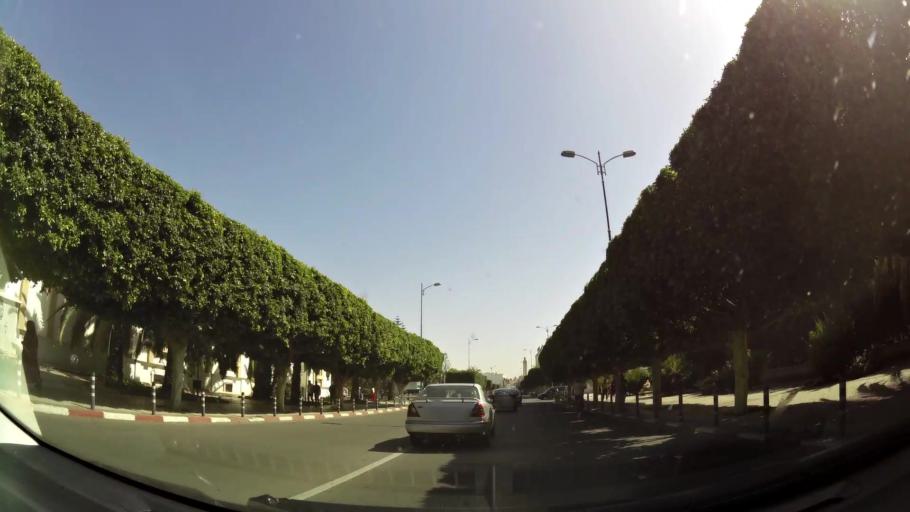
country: MA
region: Souss-Massa-Draa
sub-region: Inezgane-Ait Mellou
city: Inezgane
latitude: 30.3613
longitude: -9.5335
